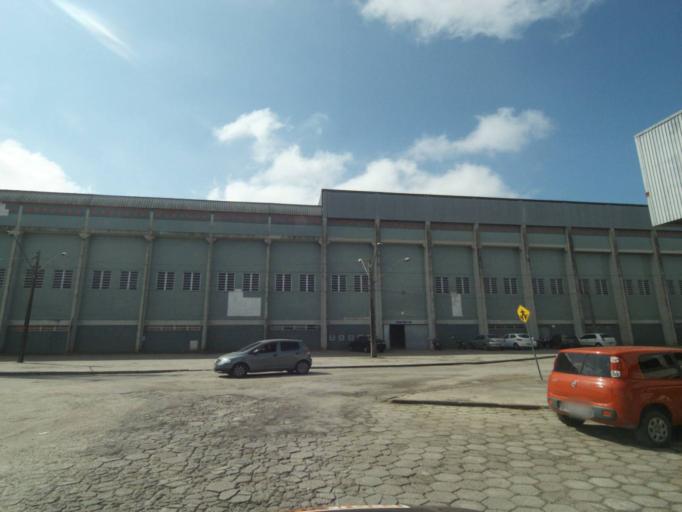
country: BR
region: Parana
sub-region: Paranagua
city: Paranagua
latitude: -25.5247
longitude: -48.5093
